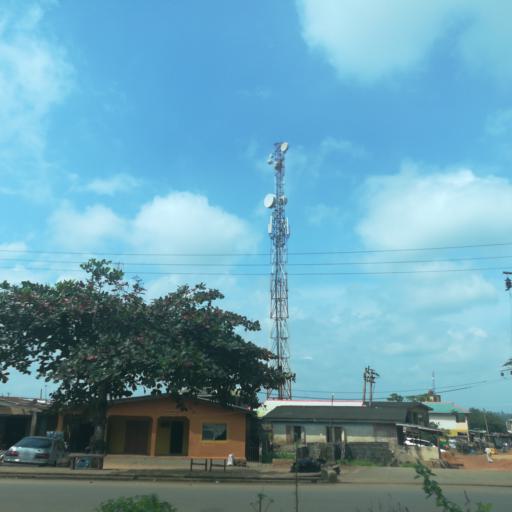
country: NG
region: Lagos
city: Ikorodu
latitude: 6.6691
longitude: 3.6722
